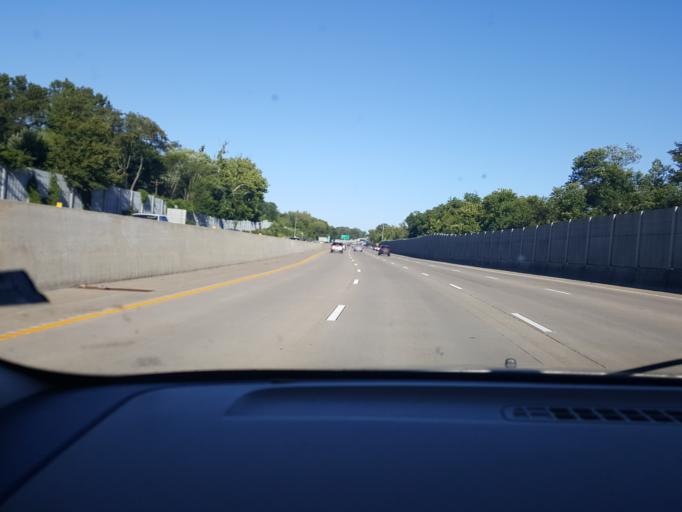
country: US
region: Missouri
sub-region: Saint Louis County
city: Ladue
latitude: 38.6318
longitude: -90.3845
